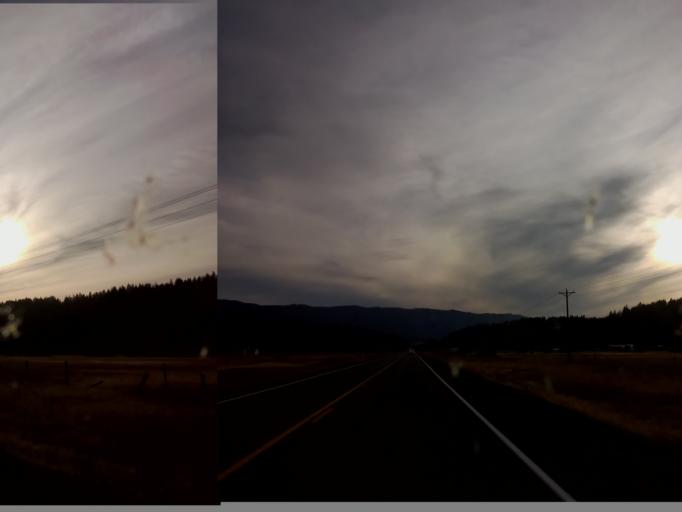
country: US
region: Washington
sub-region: Kittitas County
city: Cle Elum
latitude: 47.1912
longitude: -120.8123
